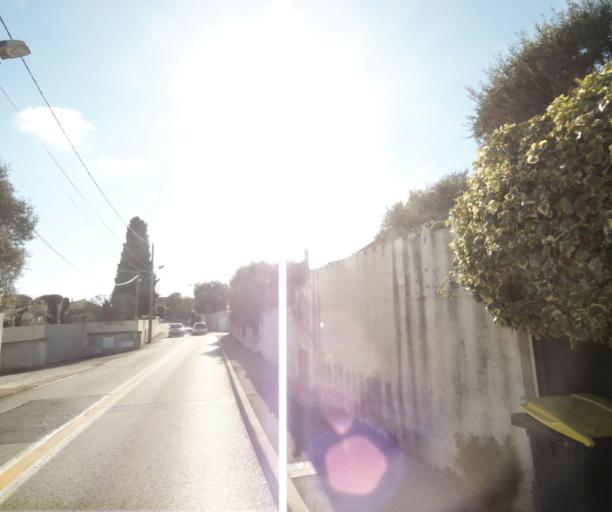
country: FR
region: Provence-Alpes-Cote d'Azur
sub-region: Departement des Alpes-Maritimes
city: Biot
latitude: 43.6020
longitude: 7.1066
